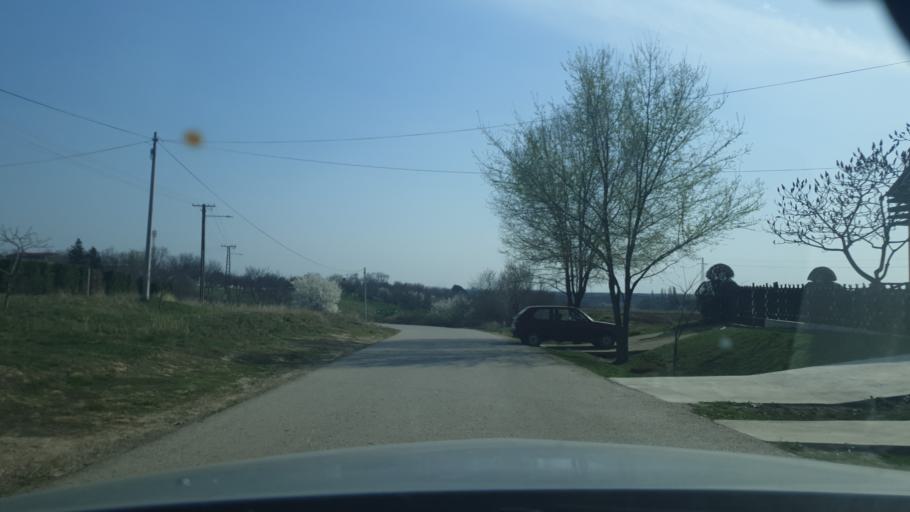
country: RS
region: Autonomna Pokrajina Vojvodina
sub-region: Sremski Okrug
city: Irig
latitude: 45.0670
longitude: 19.9216
